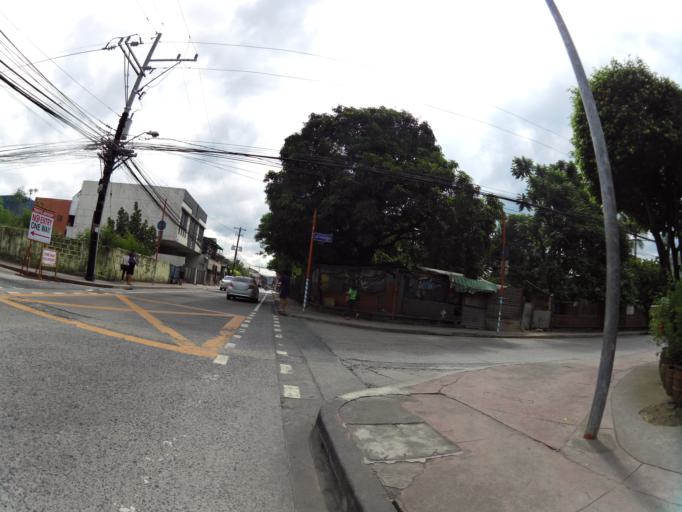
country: PH
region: Calabarzon
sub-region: Province of Rizal
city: Antipolo
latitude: 14.6418
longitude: 121.1116
